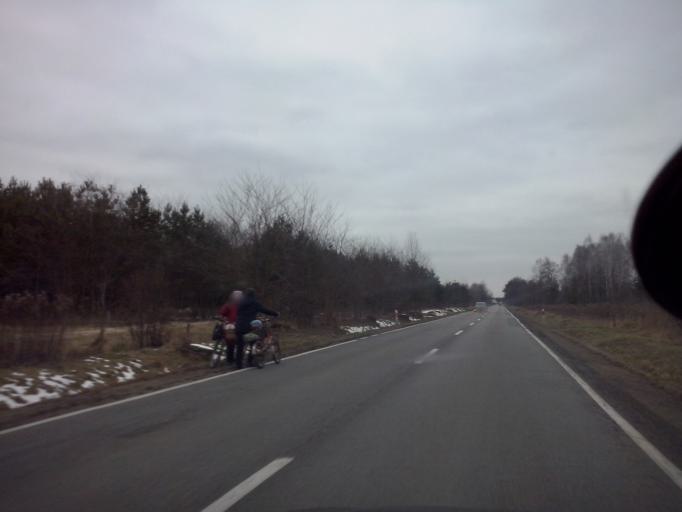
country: PL
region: Subcarpathian Voivodeship
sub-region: Powiat nizanski
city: Bieliny
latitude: 50.4102
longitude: 22.2858
